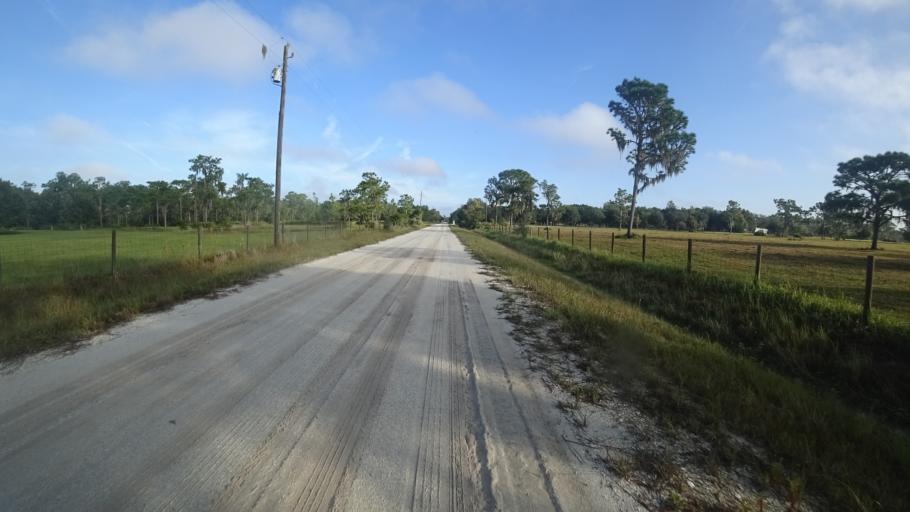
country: US
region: Florida
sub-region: Sarasota County
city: The Meadows
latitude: 27.4078
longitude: -82.2916
